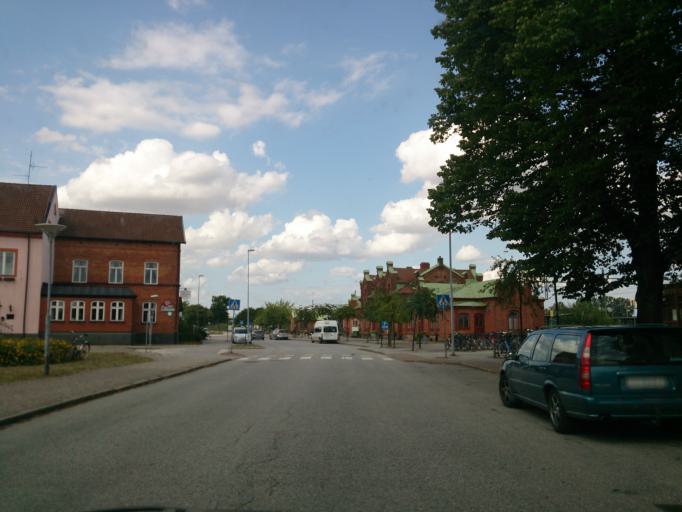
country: SE
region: Skane
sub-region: Kavlinge Kommun
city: Kaevlinge
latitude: 55.7936
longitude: 13.1104
